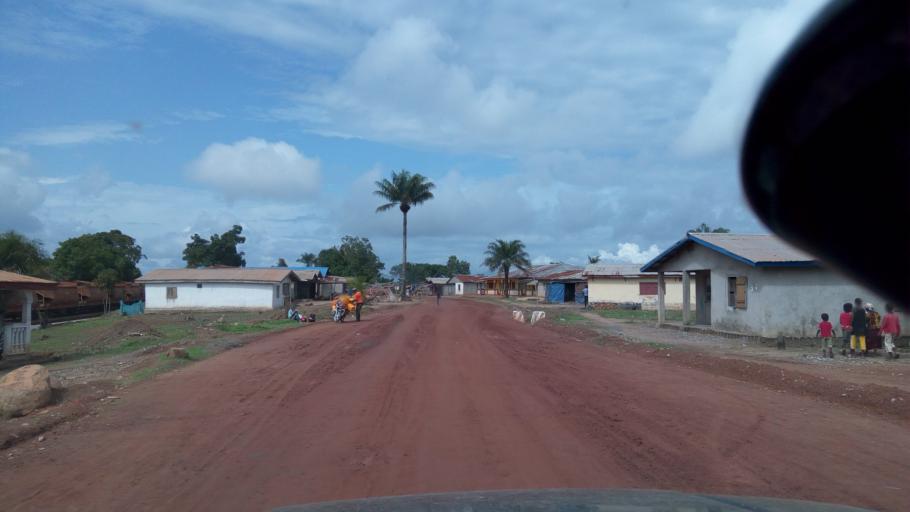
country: SL
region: Northern Province
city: Pepel
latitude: 8.5991
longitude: -13.0560
